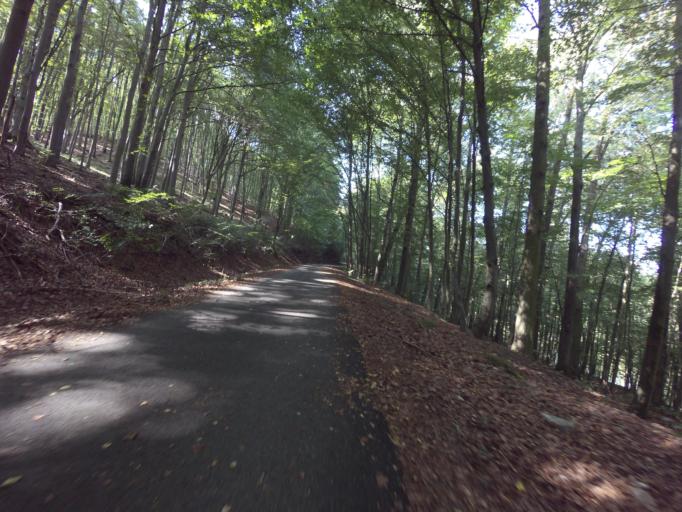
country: CZ
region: Jihocesky
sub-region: Okres Ceske Budejovice
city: Hluboka nad Vltavou
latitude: 49.0869
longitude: 14.4664
